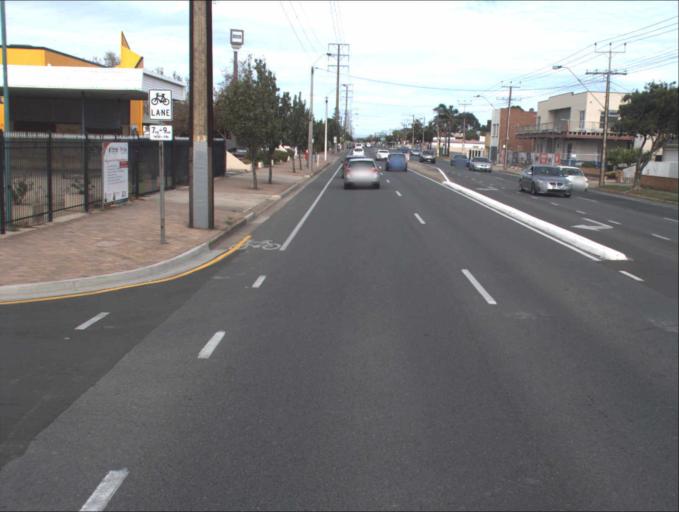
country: AU
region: South Australia
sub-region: Charles Sturt
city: Royal Park
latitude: -34.8759
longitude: 138.5126
